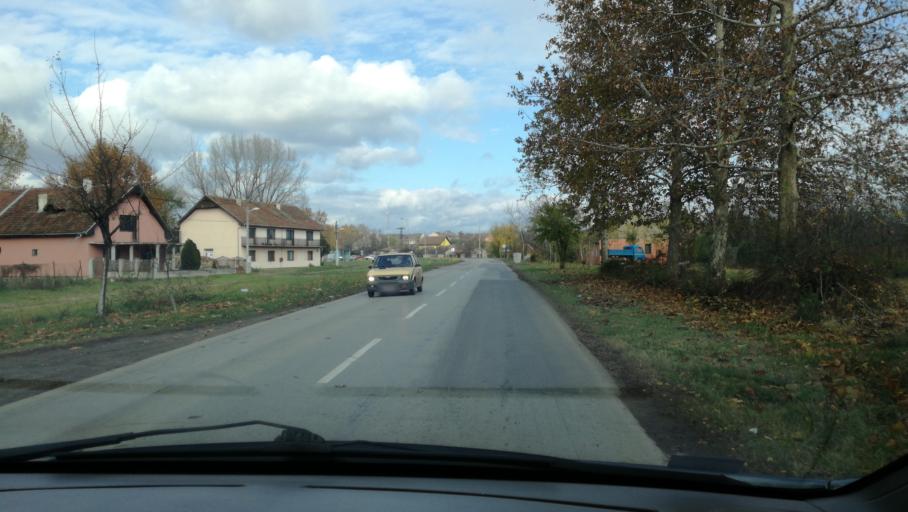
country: RS
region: Autonomna Pokrajina Vojvodina
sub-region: Severnobanatski Okrug
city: Kikinda
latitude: 45.8128
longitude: 20.4488
